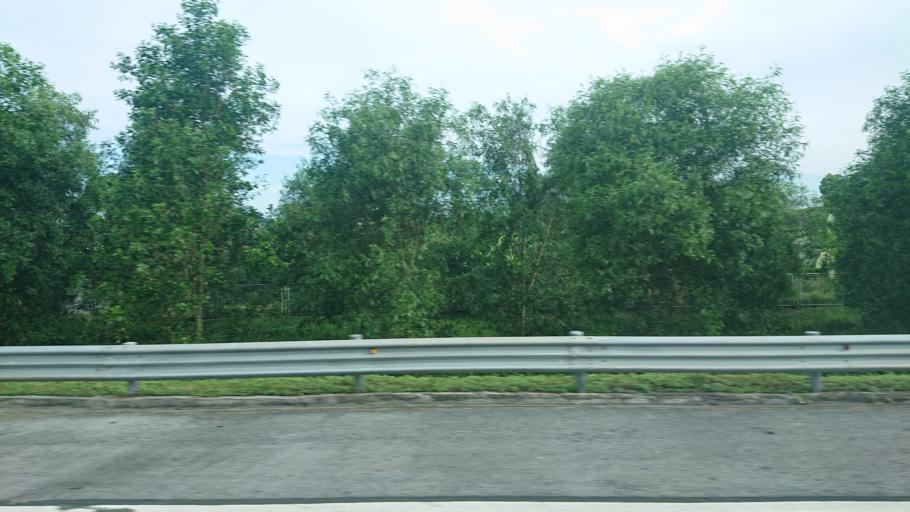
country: VN
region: Hai Phong
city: Nui Doi
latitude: 20.7655
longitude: 106.6612
